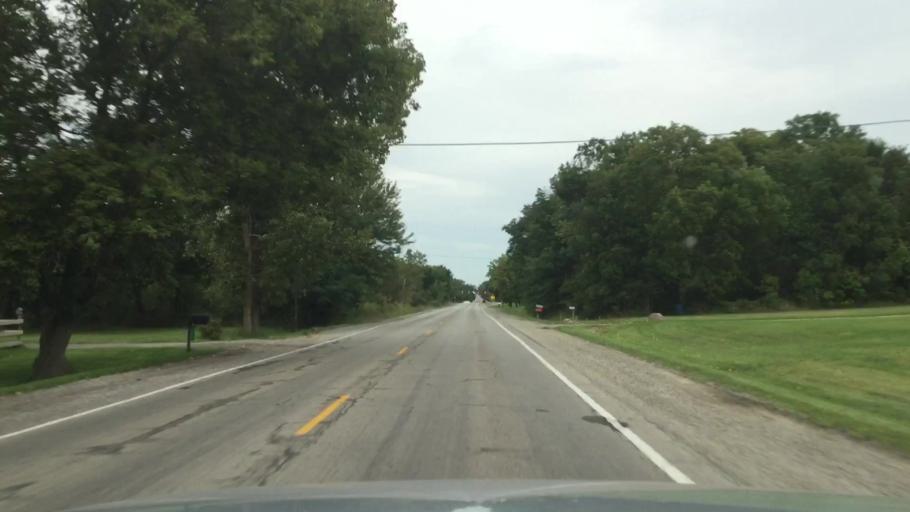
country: US
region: Michigan
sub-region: Genesee County
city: Lake Fenton
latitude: 42.8857
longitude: -83.7035
